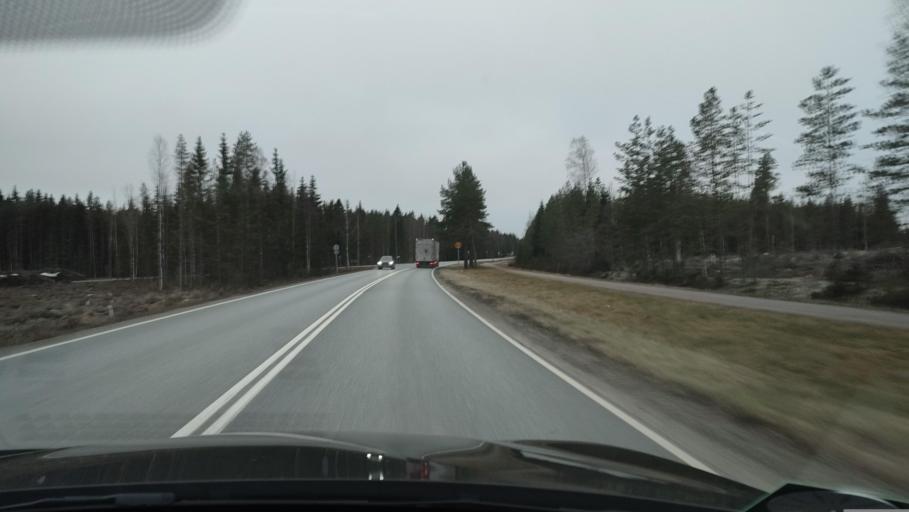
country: FI
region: Southern Ostrobothnia
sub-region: Suupohja
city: Kauhajoki
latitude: 62.3947
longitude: 22.1554
